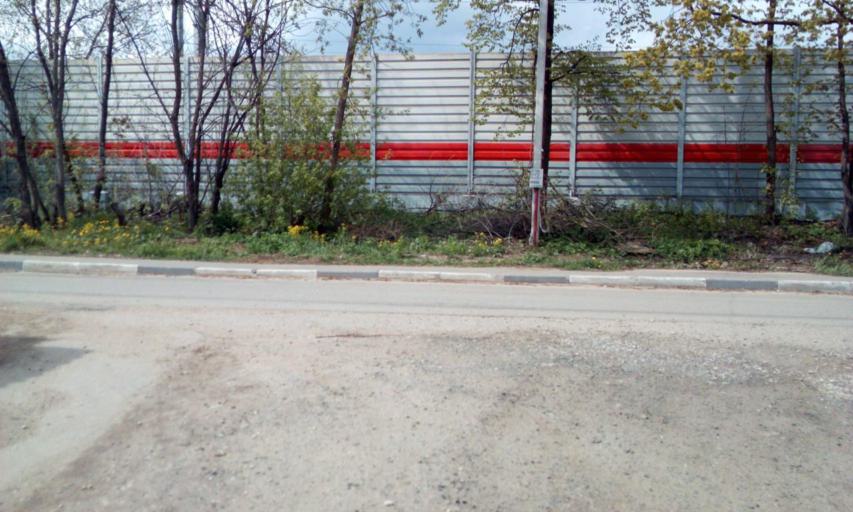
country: RU
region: Moskovskaya
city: Odintsovo
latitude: 55.6827
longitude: 37.3183
